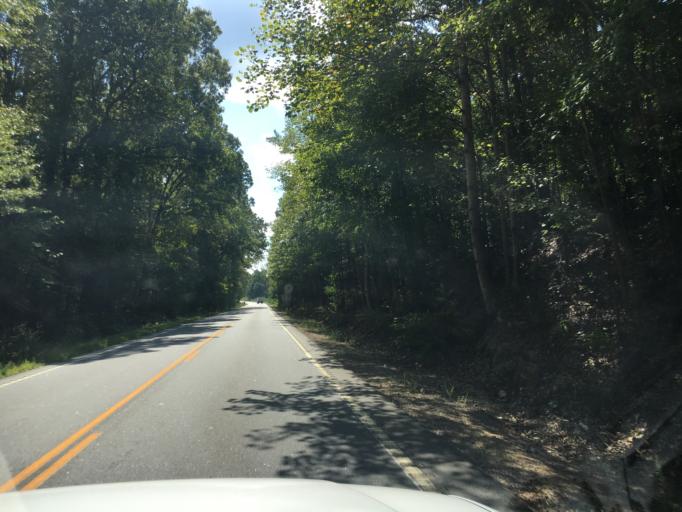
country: US
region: South Carolina
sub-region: Spartanburg County
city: Woodruff
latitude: 34.6878
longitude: -82.0650
